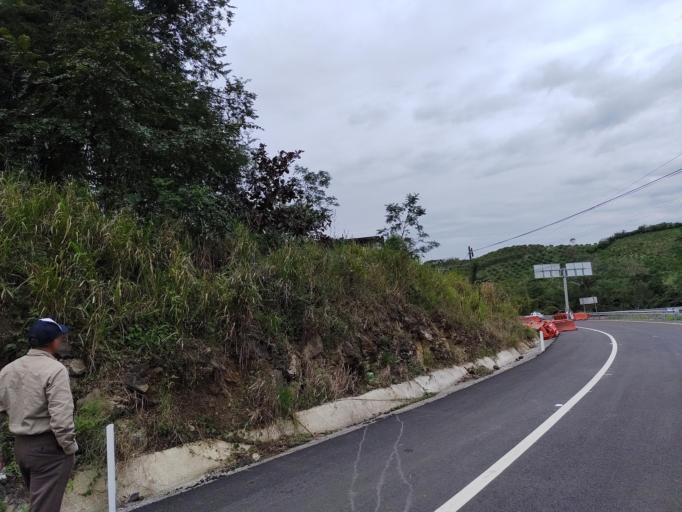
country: MX
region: Veracruz
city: Vega de San Marcos
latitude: 20.1461
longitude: -96.9477
